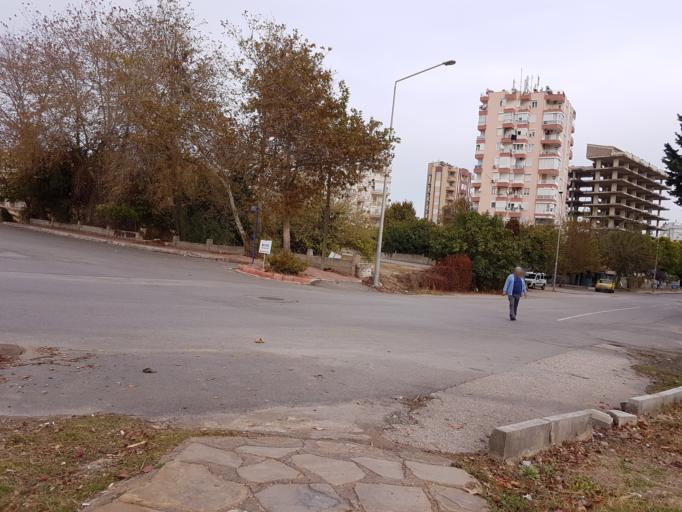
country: TR
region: Antalya
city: Antalya
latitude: 36.8534
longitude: 30.7887
